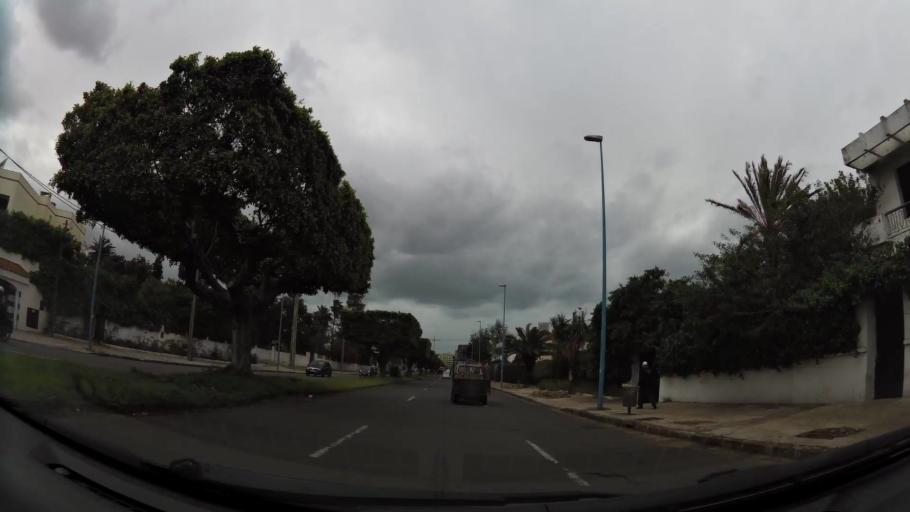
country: MA
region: Grand Casablanca
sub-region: Casablanca
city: Casablanca
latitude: 33.5620
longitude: -7.6420
